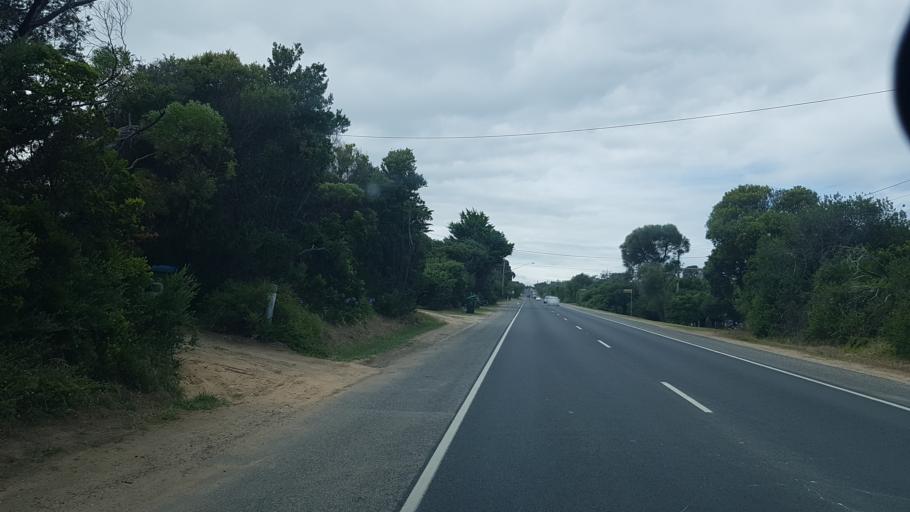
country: AU
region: Victoria
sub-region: Mornington Peninsula
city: Sorrento
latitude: -38.3491
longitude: 144.7441
